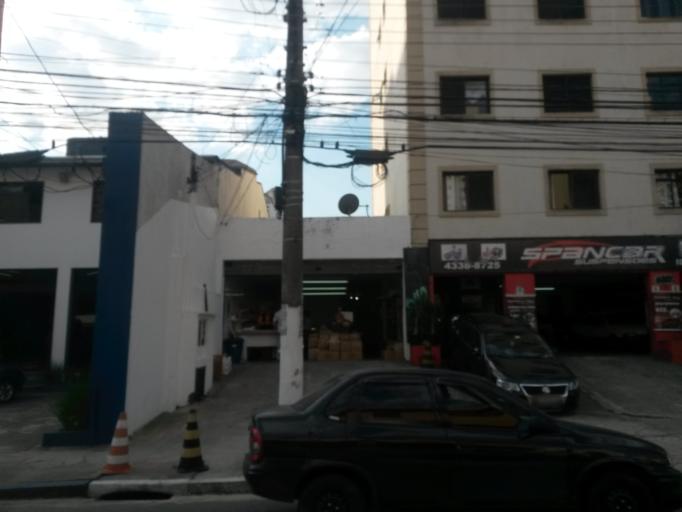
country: BR
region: Sao Paulo
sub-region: Sao Bernardo Do Campo
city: Sao Bernardo do Campo
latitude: -23.7172
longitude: -46.5543
